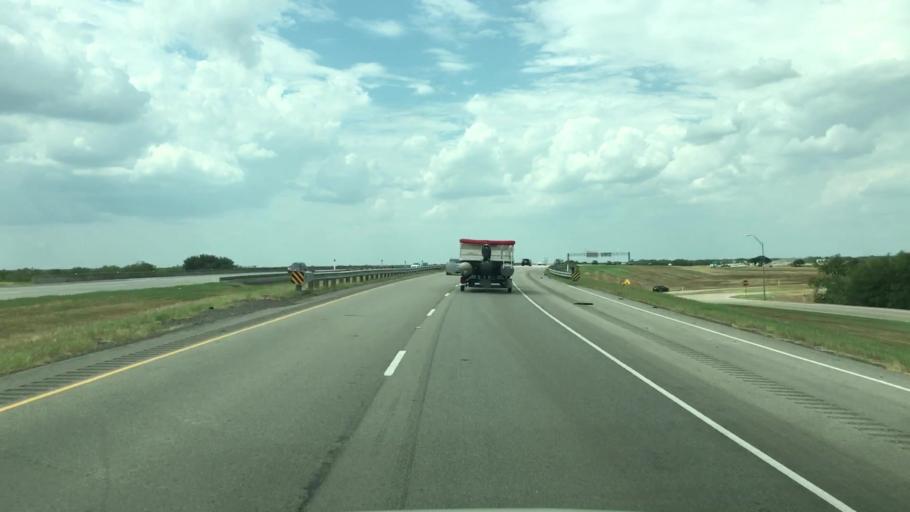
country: US
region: Texas
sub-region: Live Oak County
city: Three Rivers
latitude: 28.5246
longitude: -98.1853
